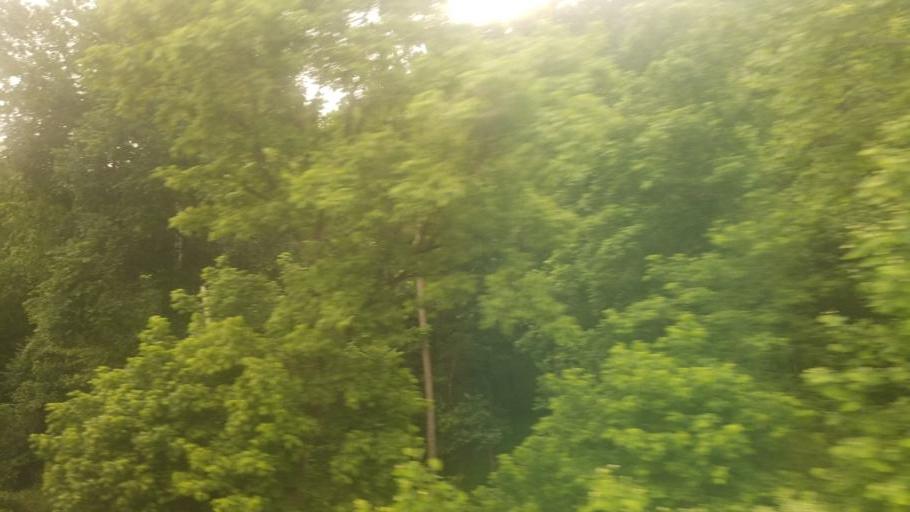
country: US
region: West Virginia
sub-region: Morgan County
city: Berkeley Springs
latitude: 39.6065
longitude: -78.3864
